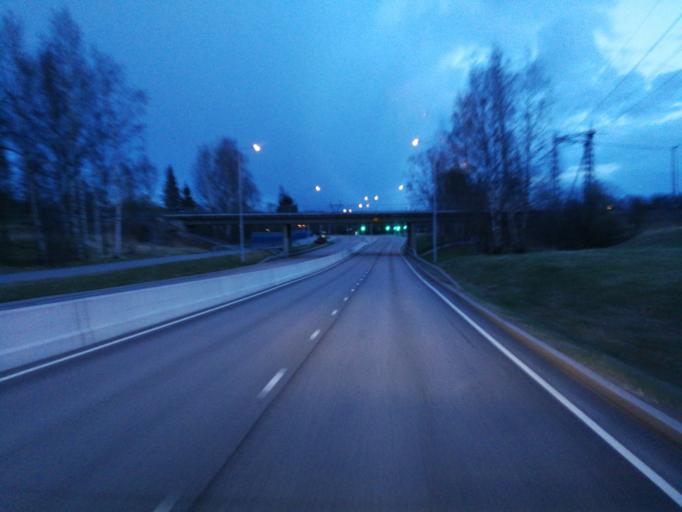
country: FI
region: Varsinais-Suomi
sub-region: Turku
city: Raisio
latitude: 60.4590
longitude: 22.1954
